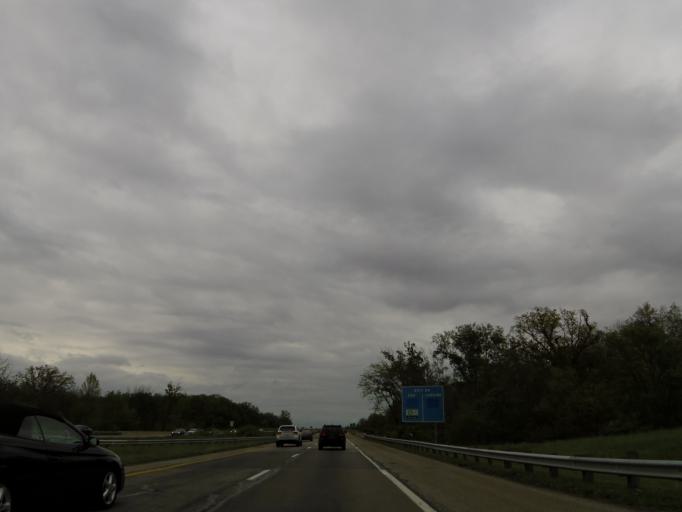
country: US
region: Ohio
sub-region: Madison County
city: Mount Sterling
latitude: 39.7472
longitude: -83.3263
